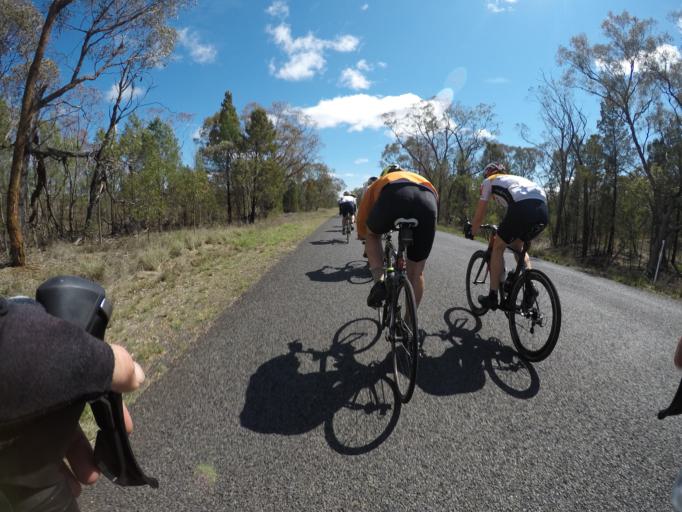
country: AU
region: New South Wales
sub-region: Parkes
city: Peak Hill
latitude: -32.6170
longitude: 148.5489
